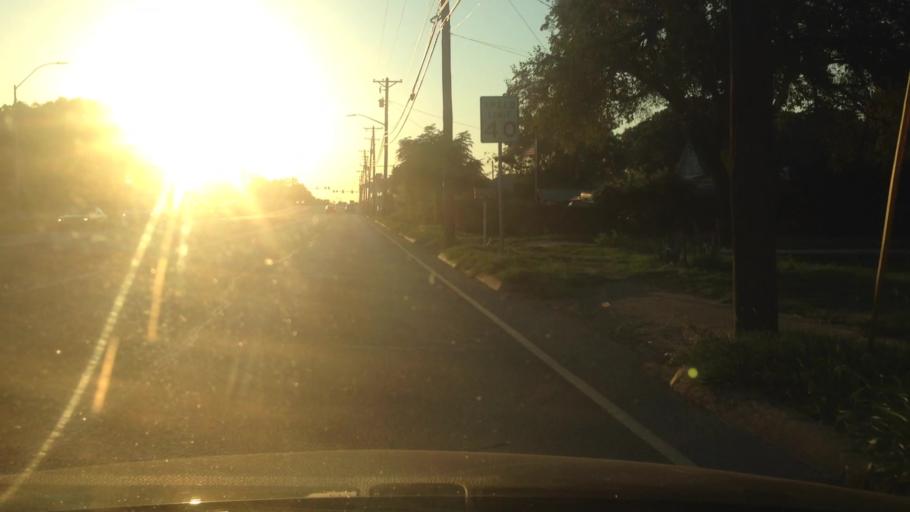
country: US
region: Texas
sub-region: Tarrant County
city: Haltom City
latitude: 32.7951
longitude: -97.2943
